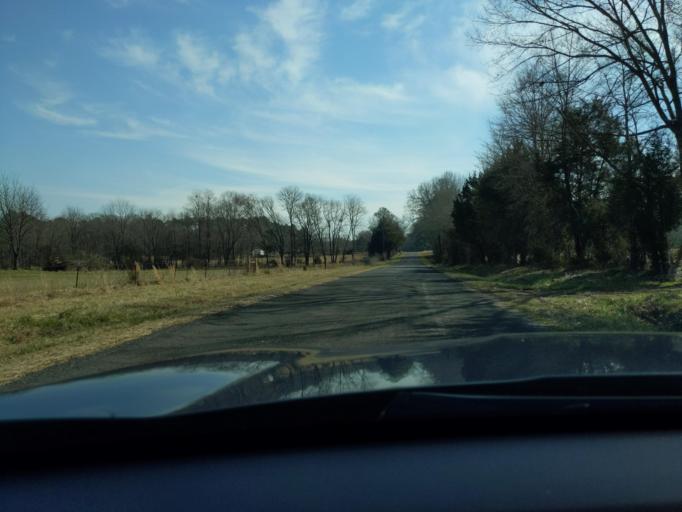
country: US
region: South Carolina
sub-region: Abbeville County
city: Calhoun Falls
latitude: 34.0943
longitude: -82.5645
